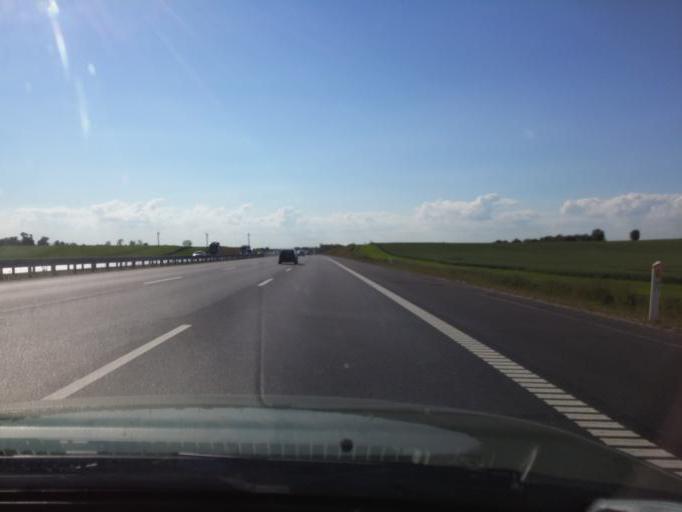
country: DK
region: South Denmark
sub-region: Middelfart Kommune
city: Norre Aby
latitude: 55.4850
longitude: 9.8567
